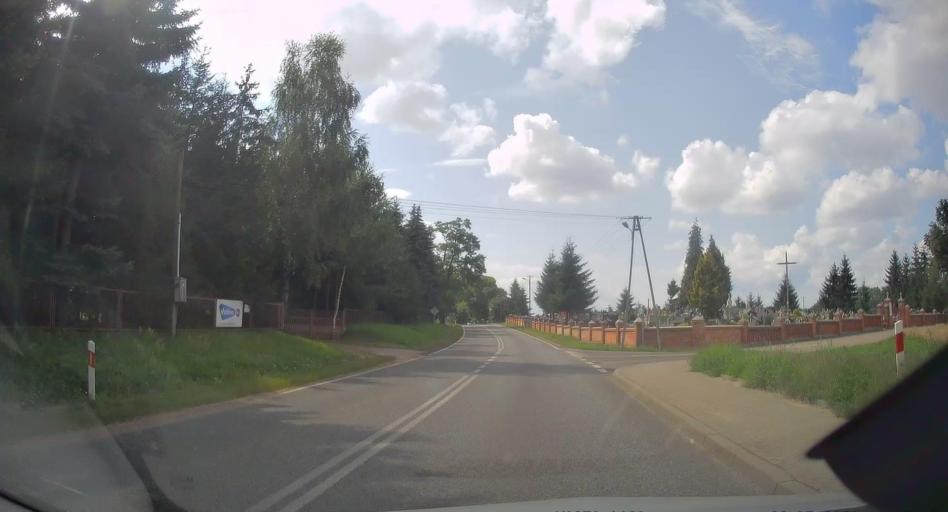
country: PL
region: Lodz Voivodeship
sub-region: Powiat brzezinski
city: Jezow
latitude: 51.8085
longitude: 20.0121
